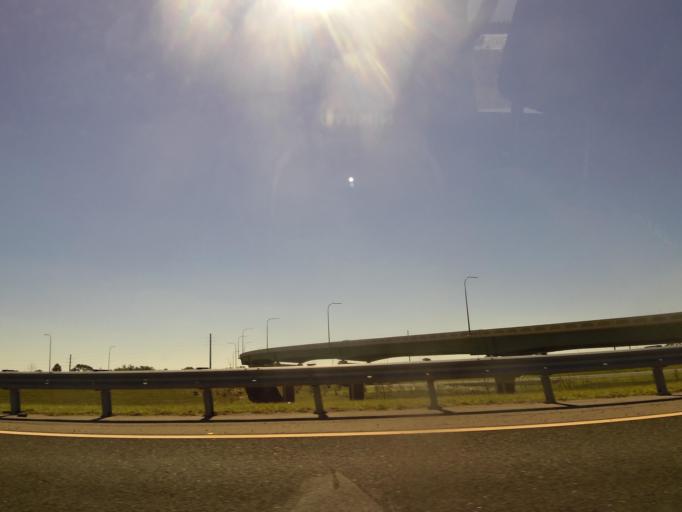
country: US
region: Florida
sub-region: Lake County
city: Mount Plymouth
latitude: 28.7740
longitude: -81.5629
